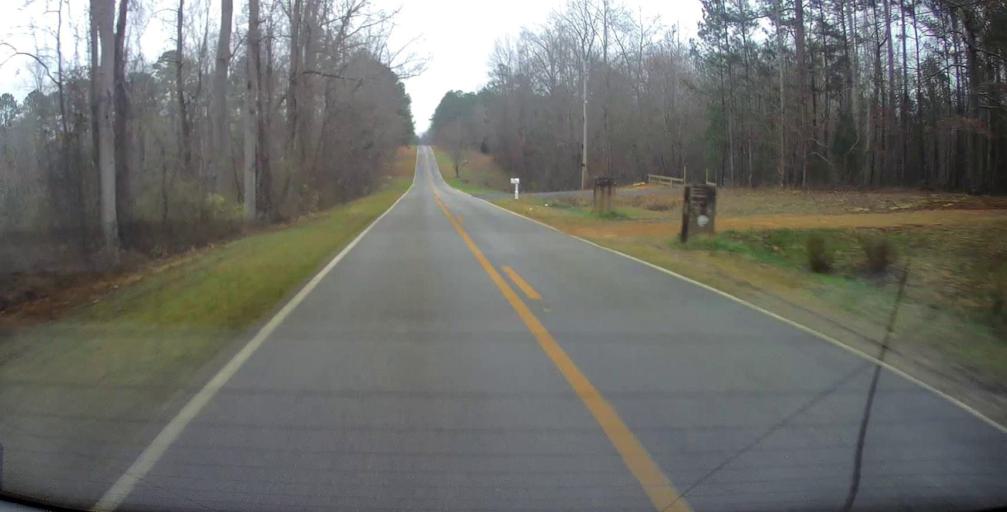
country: US
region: Georgia
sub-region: Lamar County
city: Barnesville
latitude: 33.0689
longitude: -84.1150
